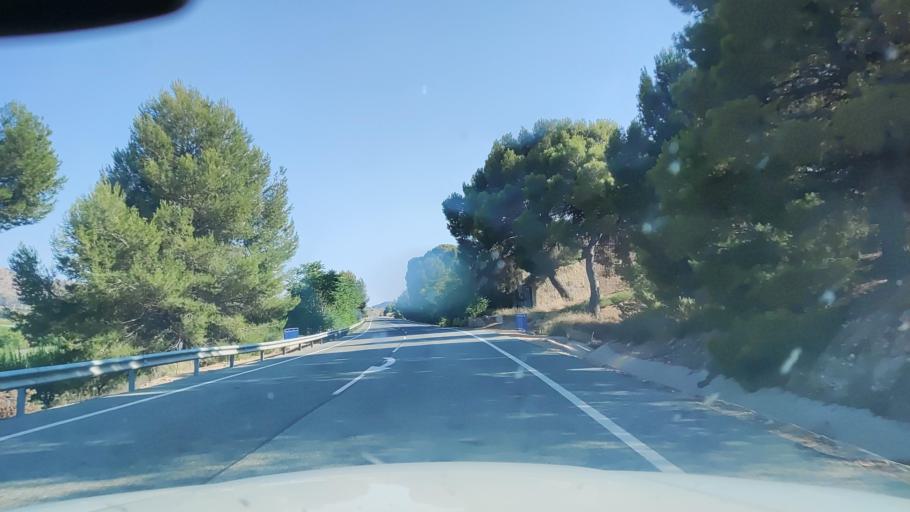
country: ES
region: Castille-La Mancha
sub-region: Provincia de Albacete
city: Tobarra
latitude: 38.6664
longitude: -1.6651
